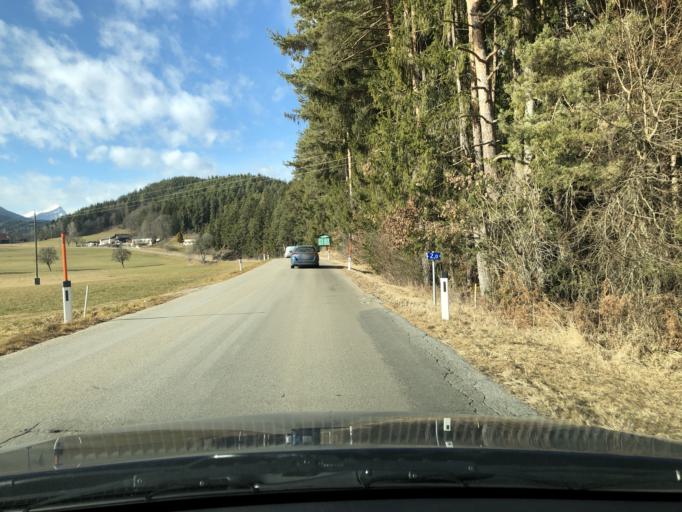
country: AT
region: Carinthia
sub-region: Politischer Bezirk Villach Land
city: Paternion
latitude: 46.7061
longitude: 13.6264
